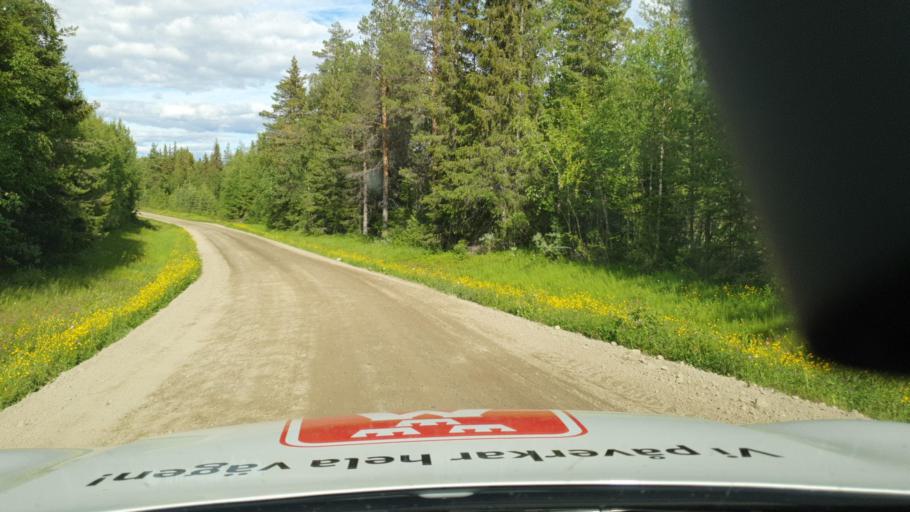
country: SE
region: Vaesterbotten
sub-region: Lycksele Kommun
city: Lycksele
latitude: 64.3285
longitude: 18.4004
